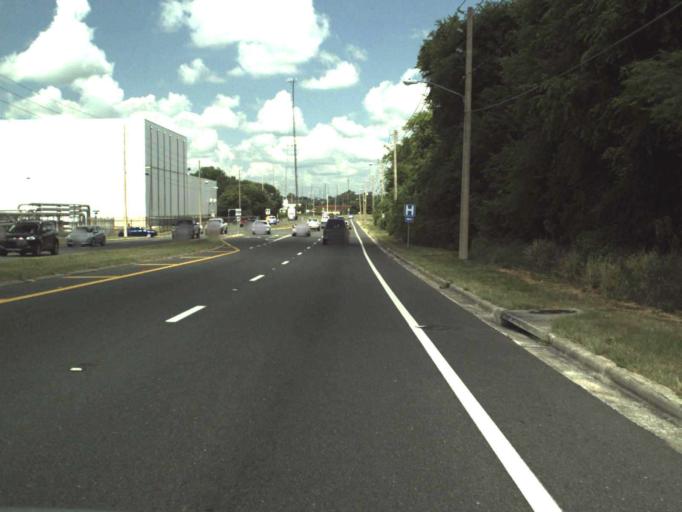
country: US
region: Florida
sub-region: Lake County
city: Leesburg
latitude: 28.8139
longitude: -81.8656
